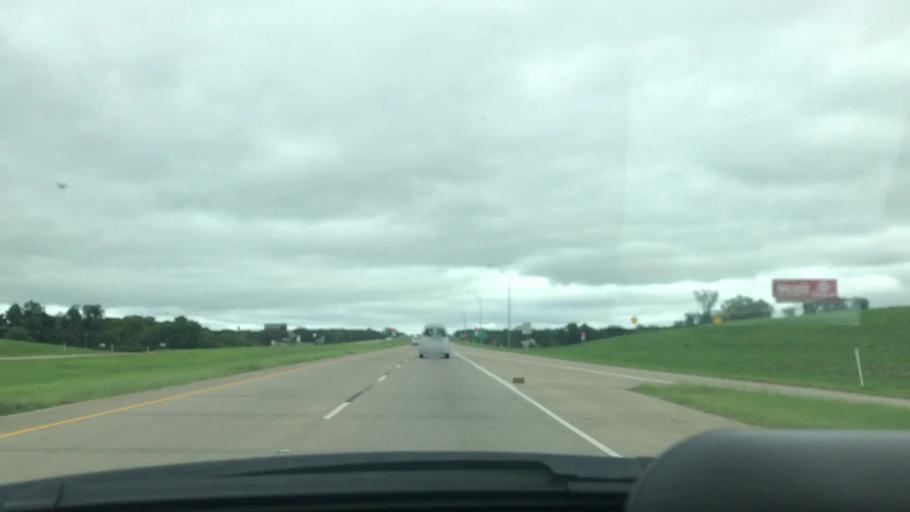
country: US
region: Texas
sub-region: Grayson County
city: Denison
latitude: 33.7229
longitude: -96.5853
